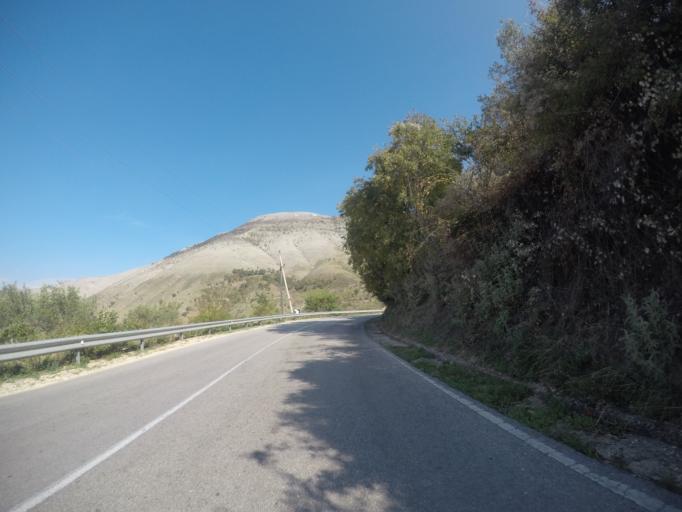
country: AL
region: Vlore
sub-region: Rrethi i Sarandes
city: Dhiver
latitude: 39.9293
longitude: 20.2019
